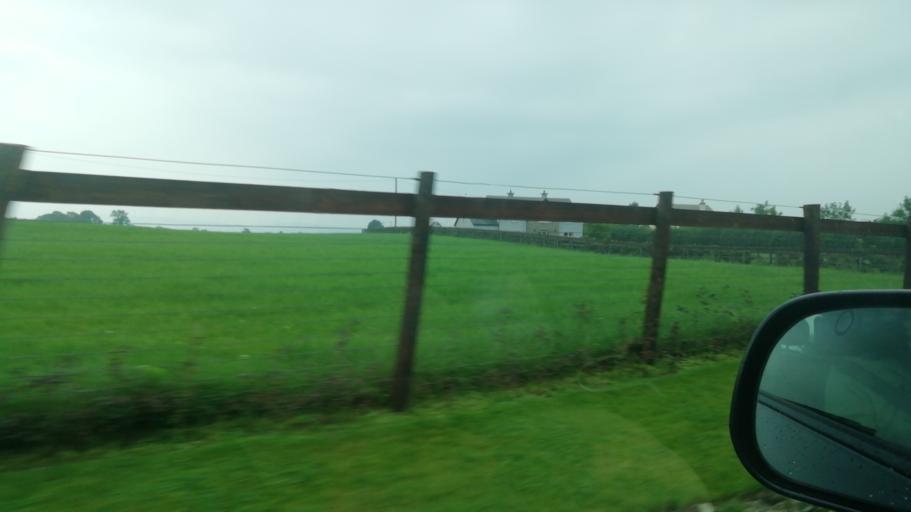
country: IE
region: Leinster
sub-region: Kilkenny
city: Thomastown
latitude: 52.6134
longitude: -7.1033
